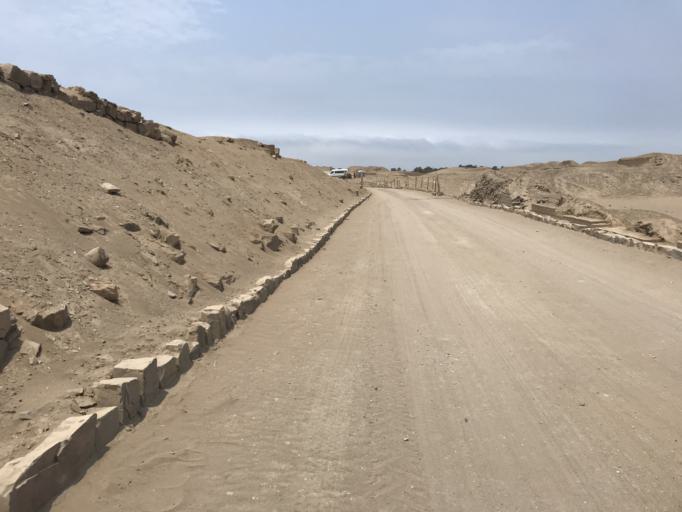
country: PE
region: Lima
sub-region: Lima
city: Punta Hermosa
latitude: -12.2588
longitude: -76.8997
